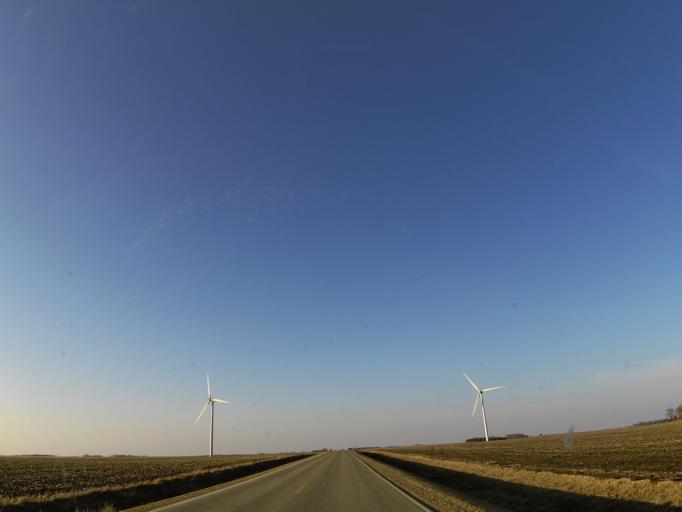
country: US
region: Iowa
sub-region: Worth County
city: Northwood
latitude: 43.4154
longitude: -93.1243
